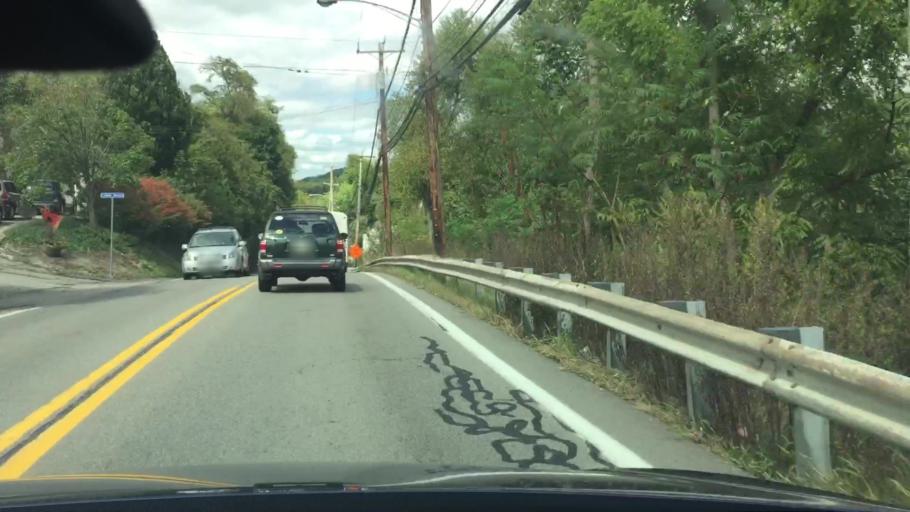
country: US
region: Pennsylvania
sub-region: Allegheny County
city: Cheswick
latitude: 40.5080
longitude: -79.7940
